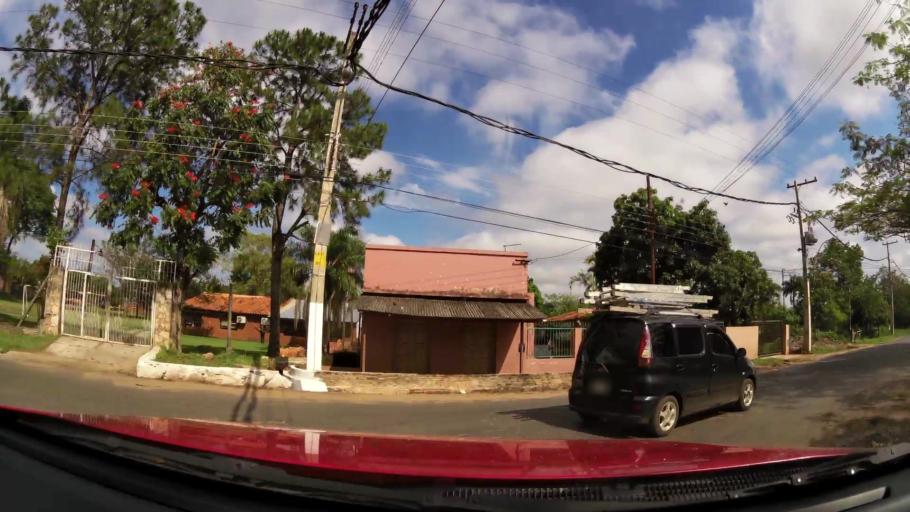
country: PY
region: Central
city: San Lorenzo
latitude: -25.2787
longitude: -57.4961
